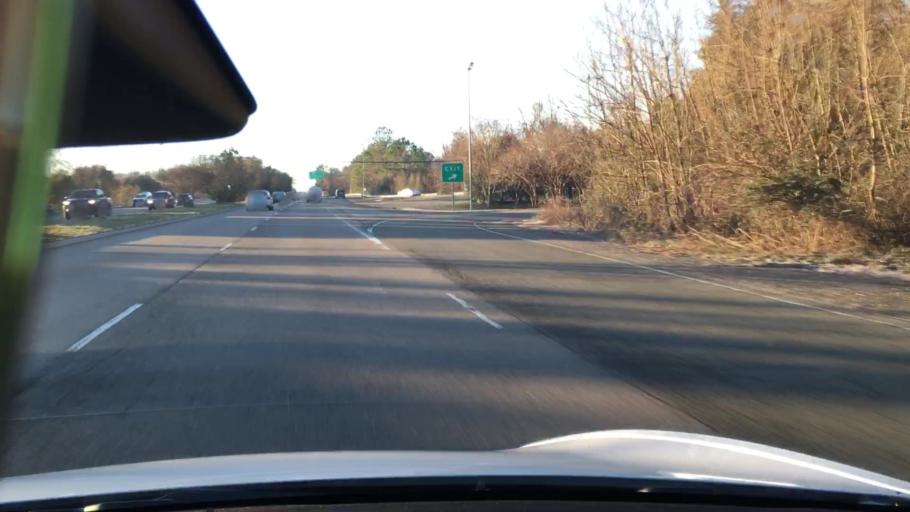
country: US
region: Virginia
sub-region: Chesterfield County
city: Bon Air
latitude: 37.5365
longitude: -77.5290
